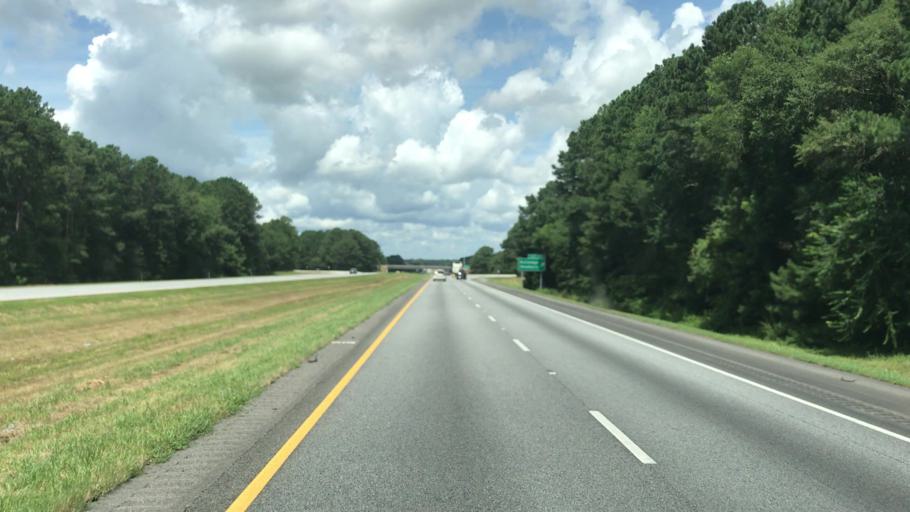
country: US
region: Georgia
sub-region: Walton County
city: Social Circle
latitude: 33.5908
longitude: -83.6234
